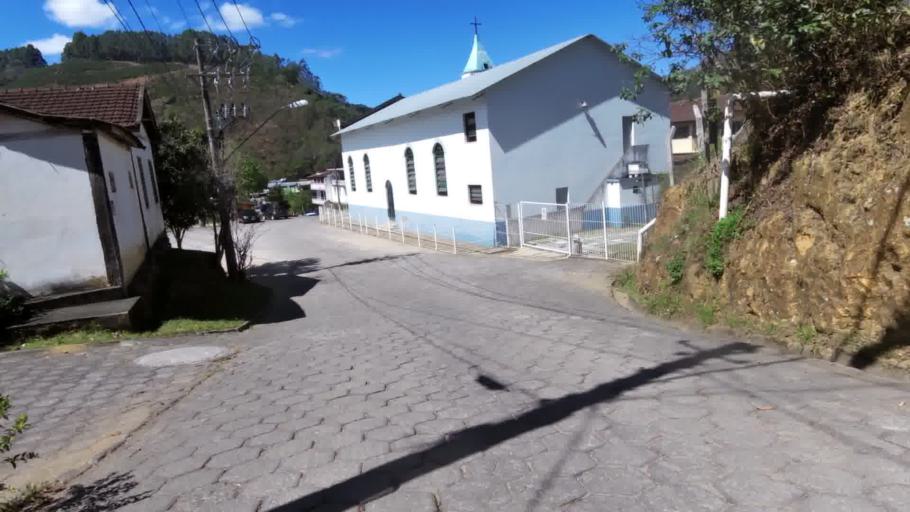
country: BR
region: Espirito Santo
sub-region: Vargem Alta
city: Vargem Alta
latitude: -20.6720
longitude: -41.0114
